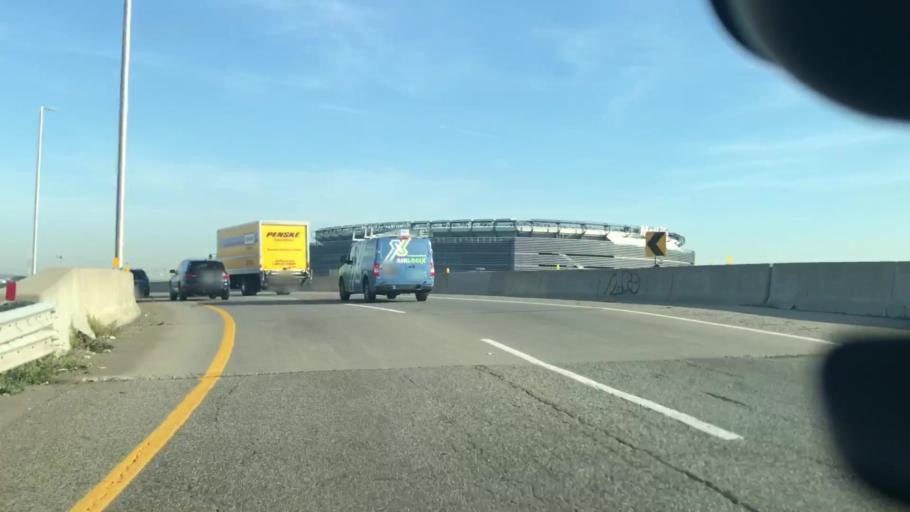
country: US
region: New Jersey
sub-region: Hudson County
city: Secaucus
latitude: 40.8089
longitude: -74.0787
